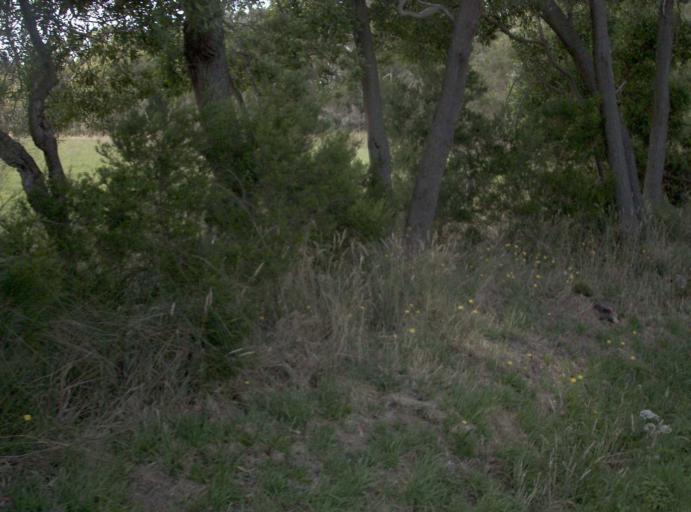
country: AU
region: Victoria
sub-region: Bass Coast
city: North Wonthaggi
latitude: -38.5694
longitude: 145.7164
